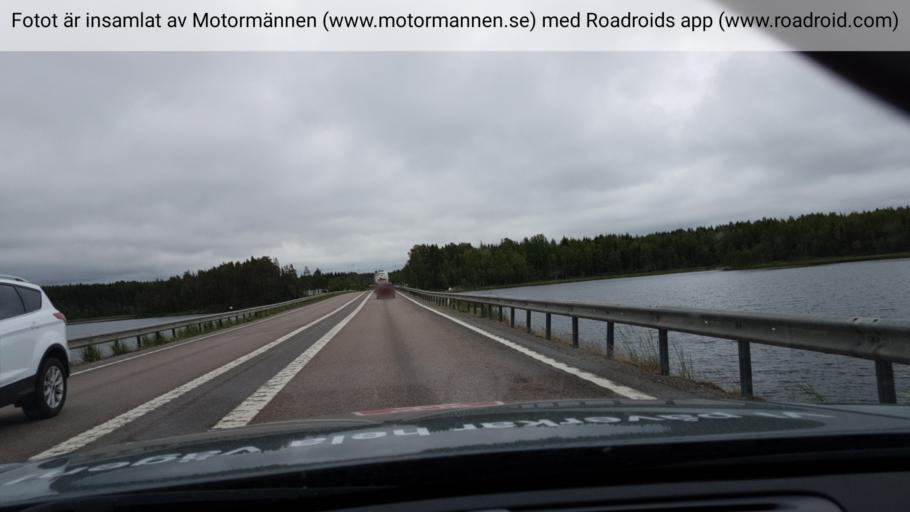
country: SE
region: Vaesternorrland
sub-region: Timra Kommun
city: Soraker
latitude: 62.5381
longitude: 17.5516
